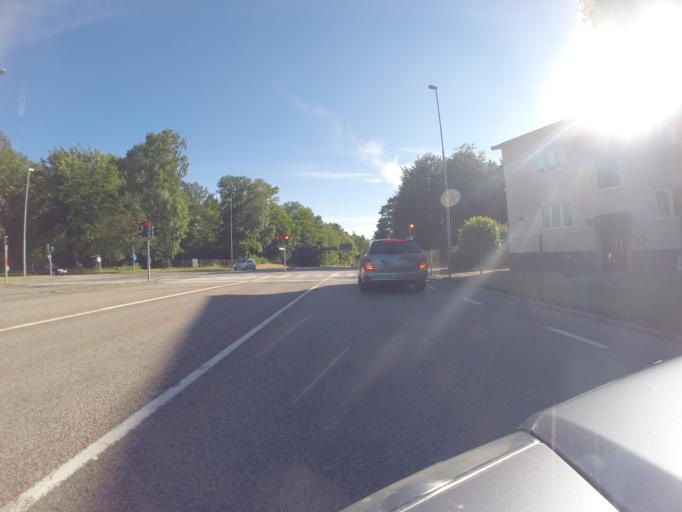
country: SE
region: Skane
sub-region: Angelholms Kommun
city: AEngelholm
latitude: 56.2375
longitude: 12.8637
